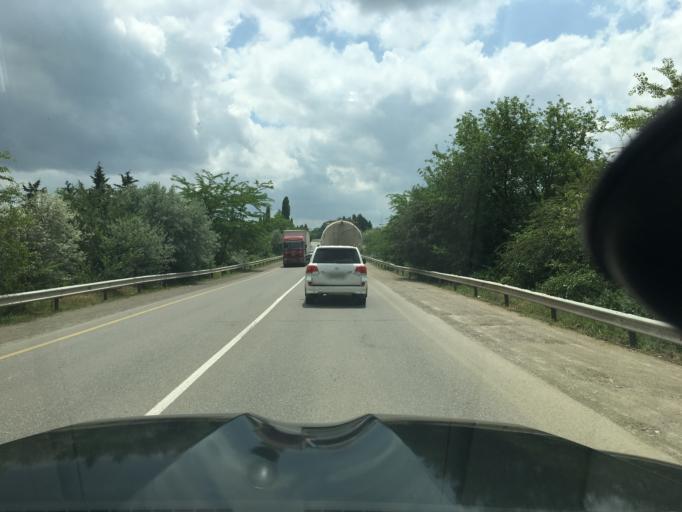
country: AZ
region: Tovuz
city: Qaraxanli
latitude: 41.0335
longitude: 45.5926
